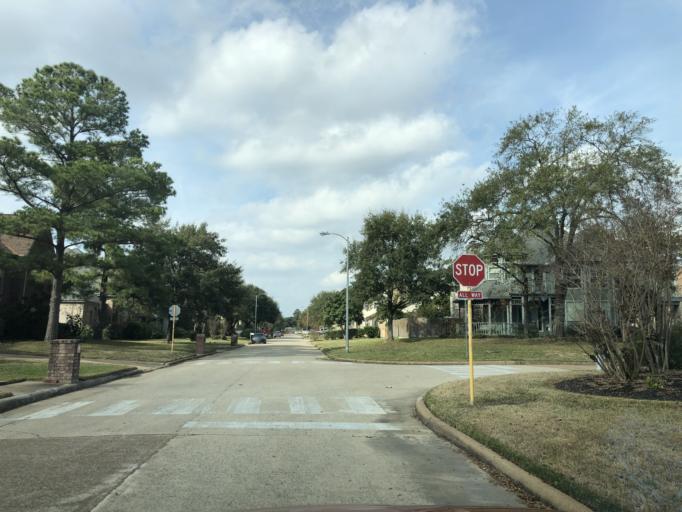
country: US
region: Texas
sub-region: Harris County
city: Tomball
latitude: 30.0322
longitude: -95.5398
